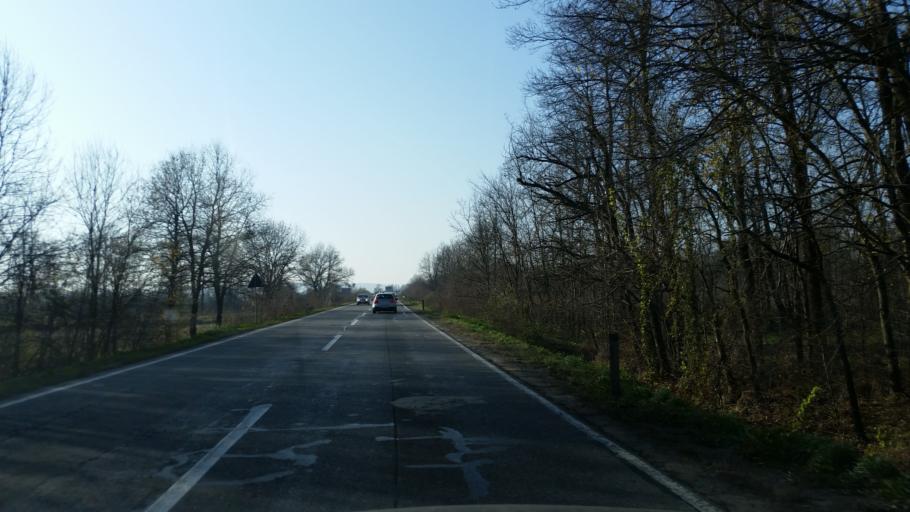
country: RS
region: Central Serbia
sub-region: Belgrade
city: Lazarevac
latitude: 44.4149
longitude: 20.2603
